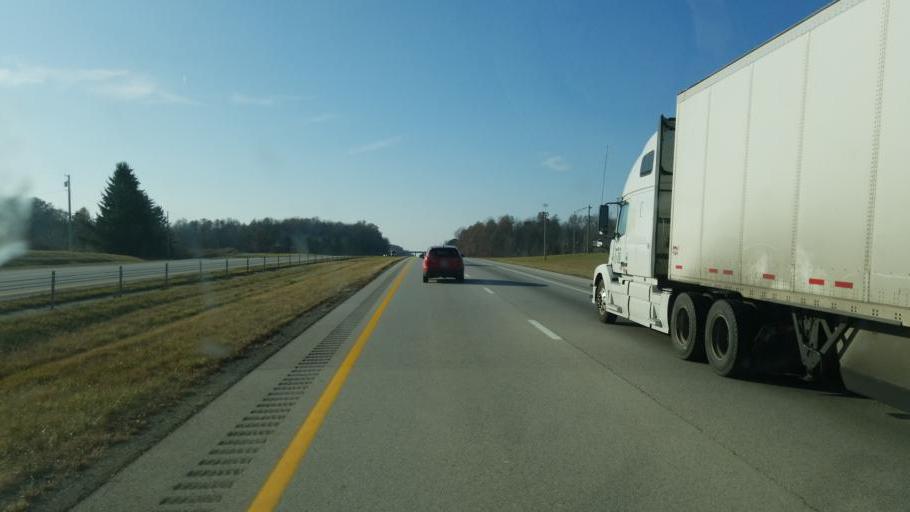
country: US
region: Ohio
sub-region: Wayne County
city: Rittman
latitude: 41.0320
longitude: -81.8003
